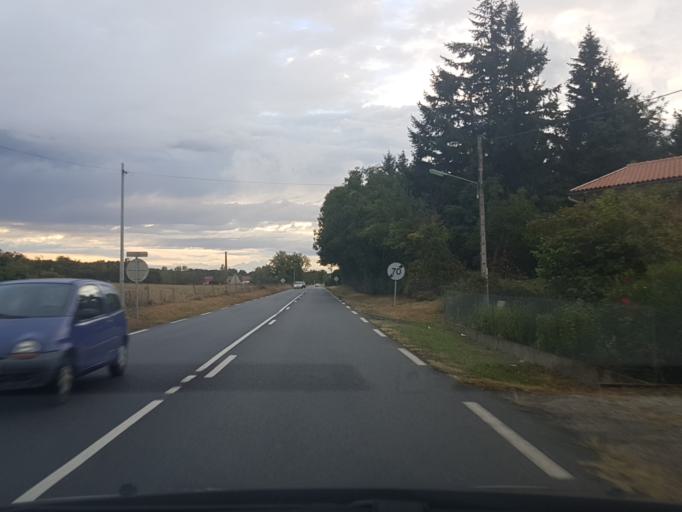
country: FR
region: Midi-Pyrenees
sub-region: Departement de l'Ariege
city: La Tour-du-Crieu
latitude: 43.0870
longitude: 1.7361
